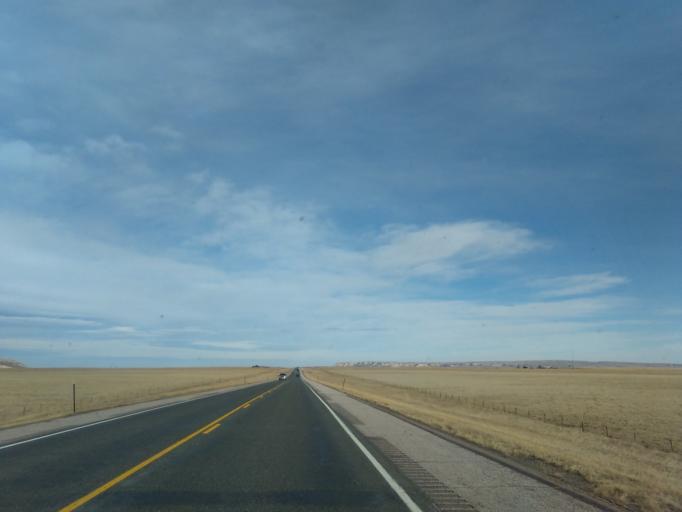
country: US
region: Wyoming
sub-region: Laramie County
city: Pine Bluffs
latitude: 41.5992
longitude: -104.2628
